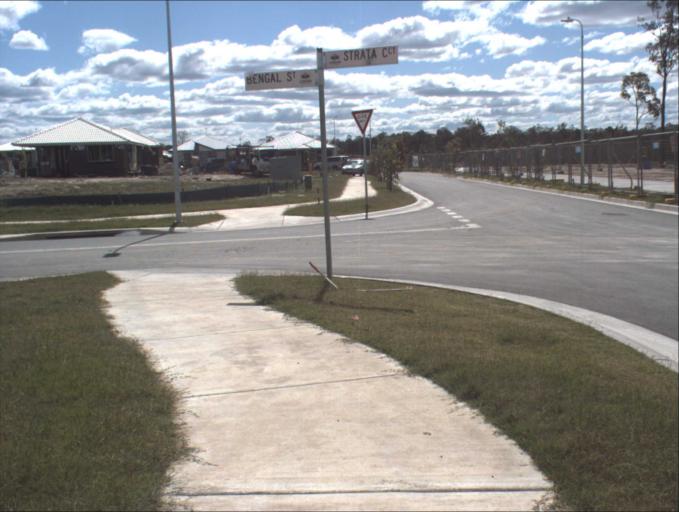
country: AU
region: Queensland
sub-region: Logan
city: Chambers Flat
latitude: -27.8013
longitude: 153.1160
